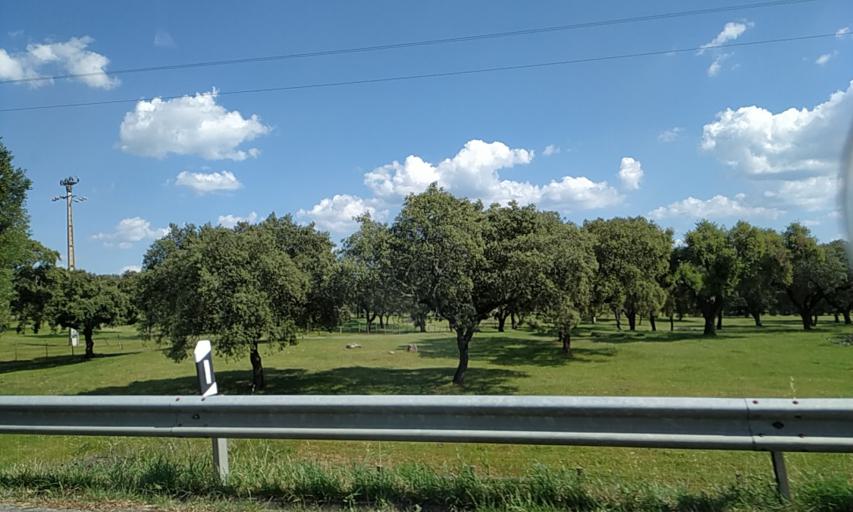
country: PT
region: Evora
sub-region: Montemor-O-Novo
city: Montemor-o-Novo
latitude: 38.6789
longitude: -8.1315
